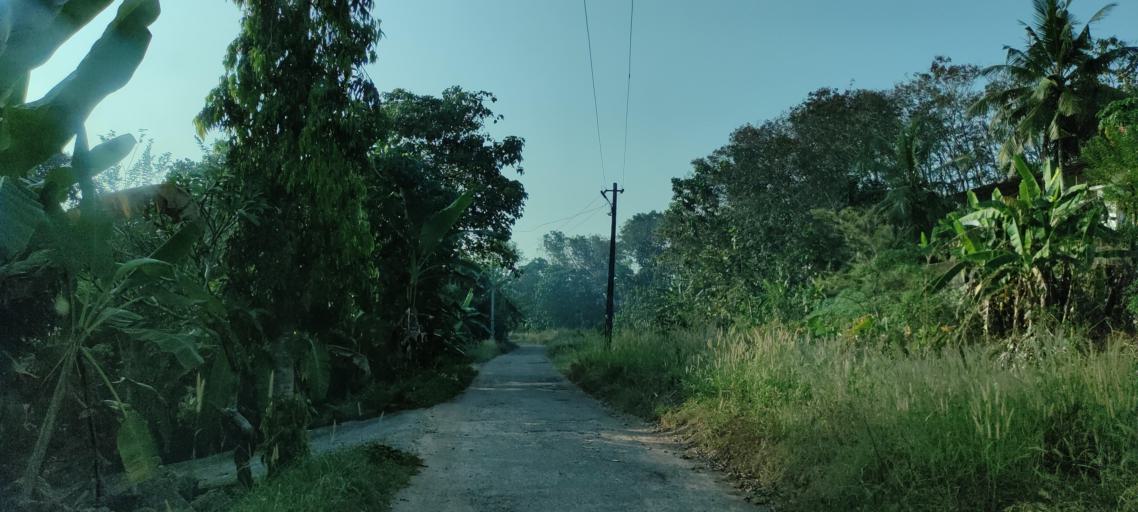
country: IN
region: Kerala
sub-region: Pattanamtitta
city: Adur
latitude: 9.1357
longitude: 76.7308
